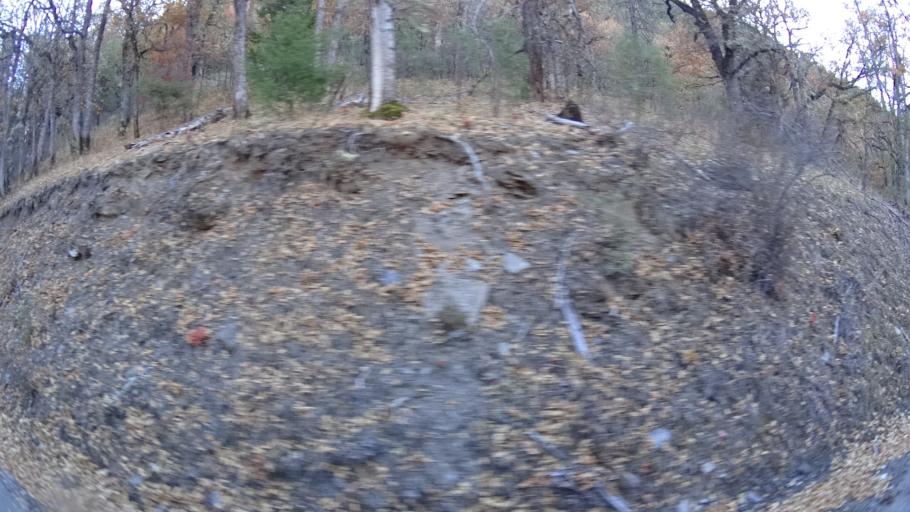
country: US
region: California
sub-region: Siskiyou County
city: Yreka
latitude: 41.8456
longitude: -122.9064
